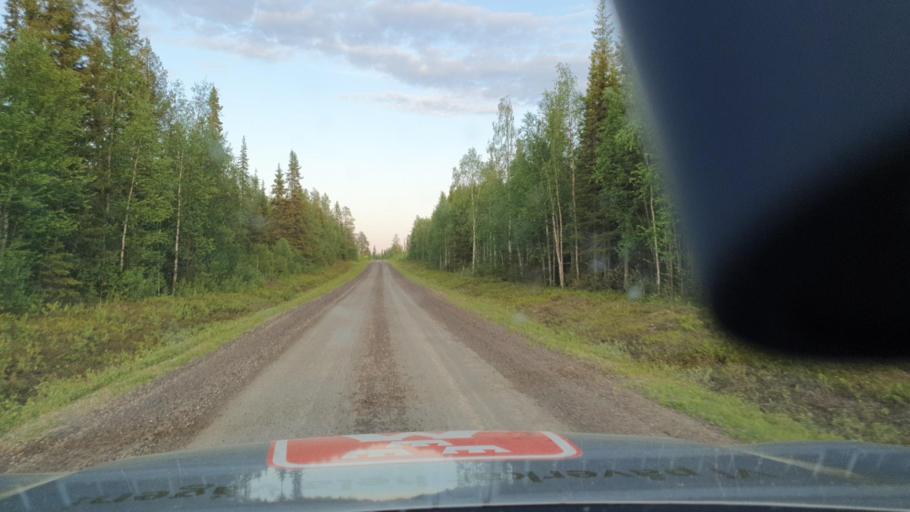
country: SE
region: Norrbotten
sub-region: Bodens Kommun
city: Boden
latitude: 66.4862
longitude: 21.5961
